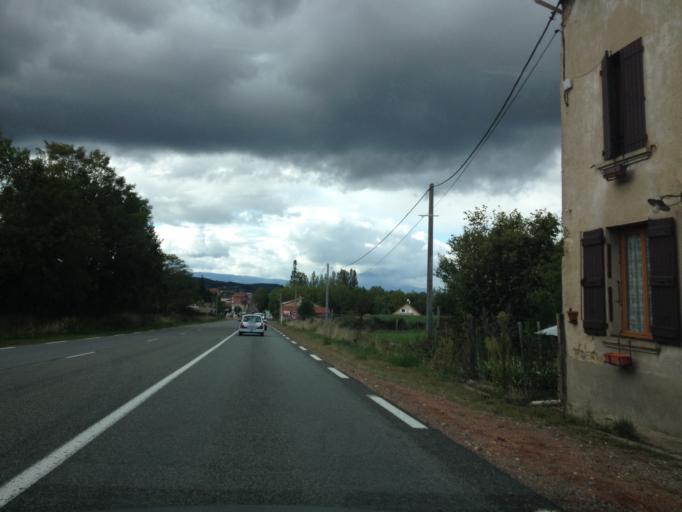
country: FR
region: Rhone-Alpes
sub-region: Departement de la Loire
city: Saint-Symphorien-de-Lay
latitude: 45.9459
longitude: 4.2247
